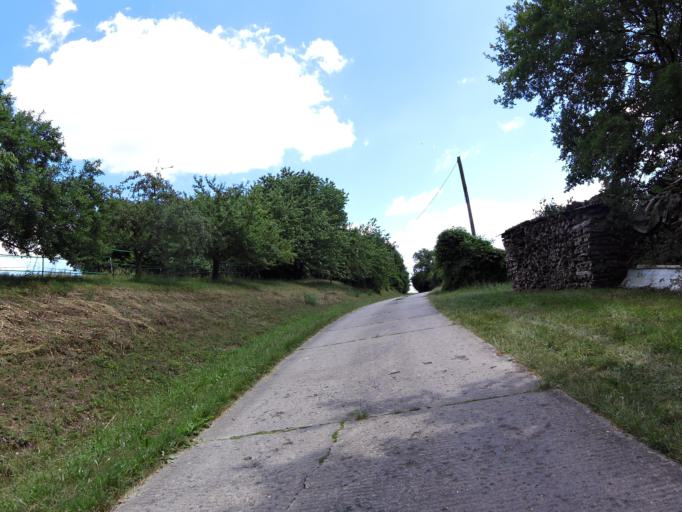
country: DE
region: Bavaria
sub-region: Regierungsbezirk Unterfranken
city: Gadheim
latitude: 49.8322
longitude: 9.9295
